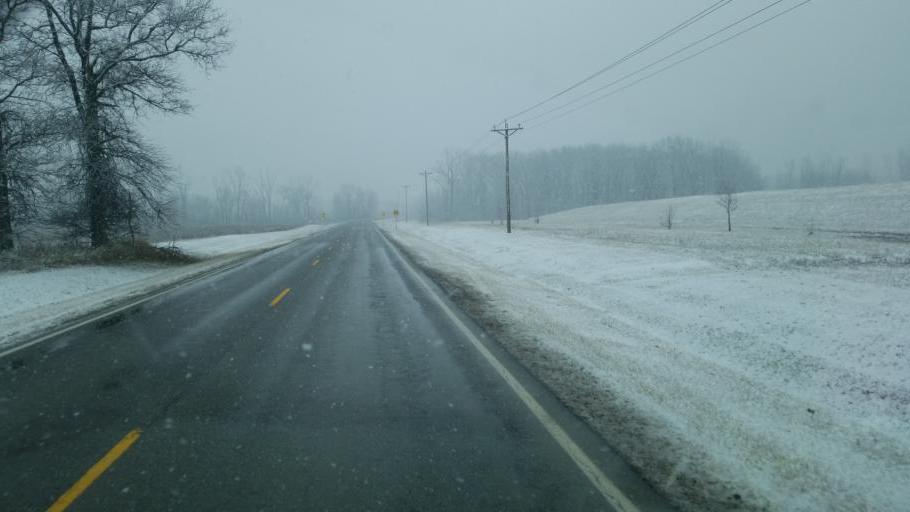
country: US
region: Ohio
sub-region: Champaign County
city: North Lewisburg
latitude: 40.2794
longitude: -83.4917
